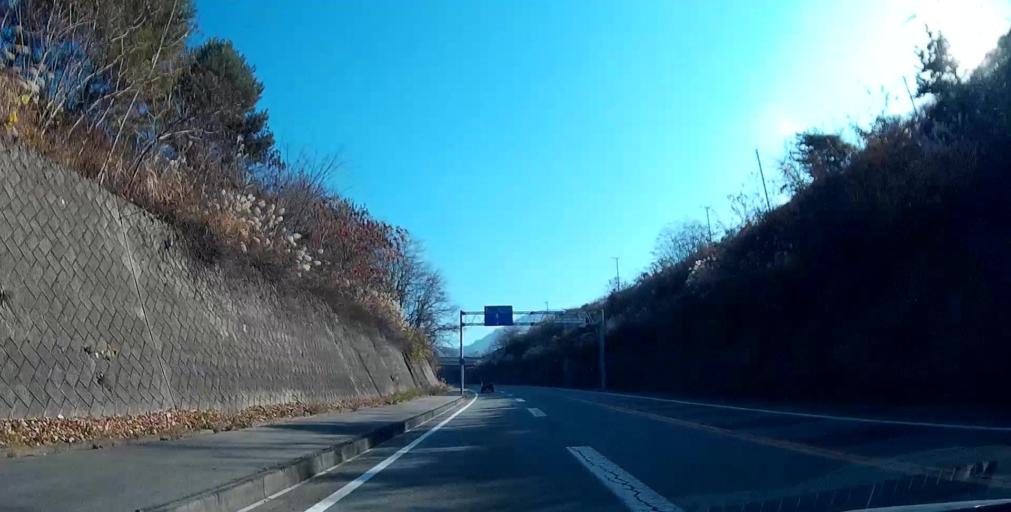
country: JP
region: Yamanashi
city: Isawa
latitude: 35.6130
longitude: 138.6966
